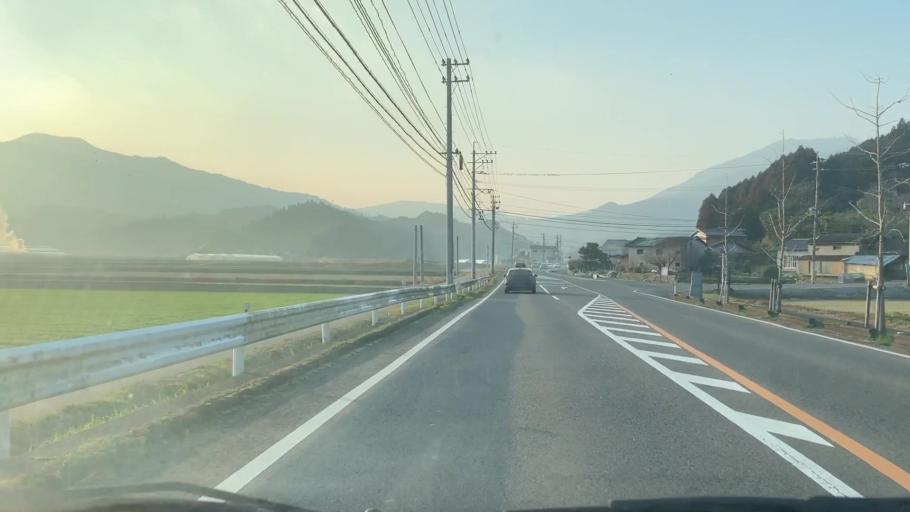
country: JP
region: Saga Prefecture
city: Takeocho-takeo
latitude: 33.2583
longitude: 130.0698
